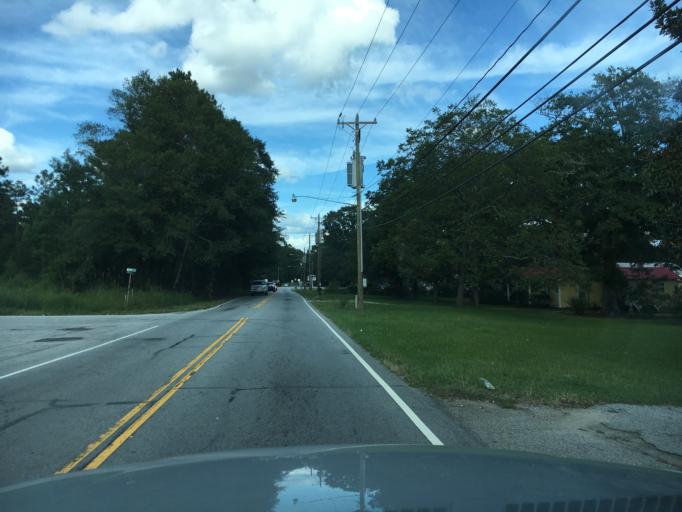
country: US
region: South Carolina
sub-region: Greenville County
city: Fountain Inn
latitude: 34.6992
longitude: -82.1851
